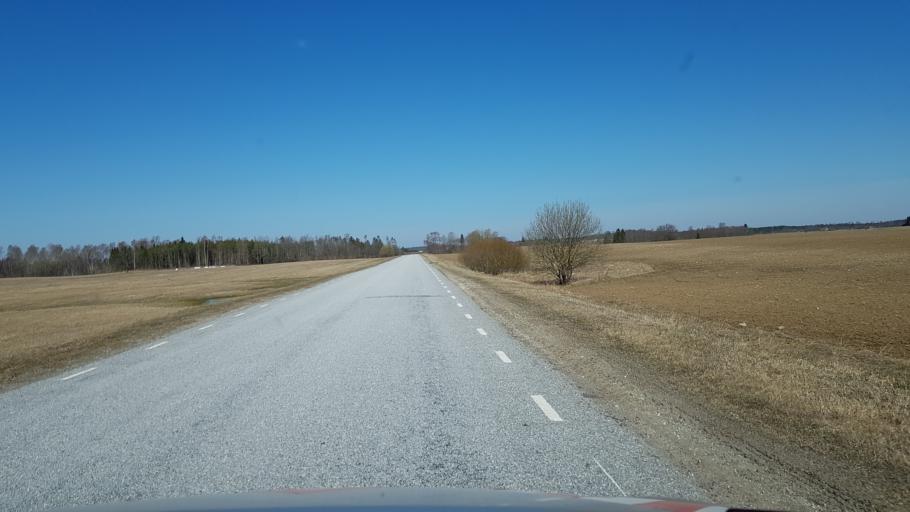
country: EE
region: Jaervamaa
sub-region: Koeru vald
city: Koeru
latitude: 59.0185
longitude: 26.0883
